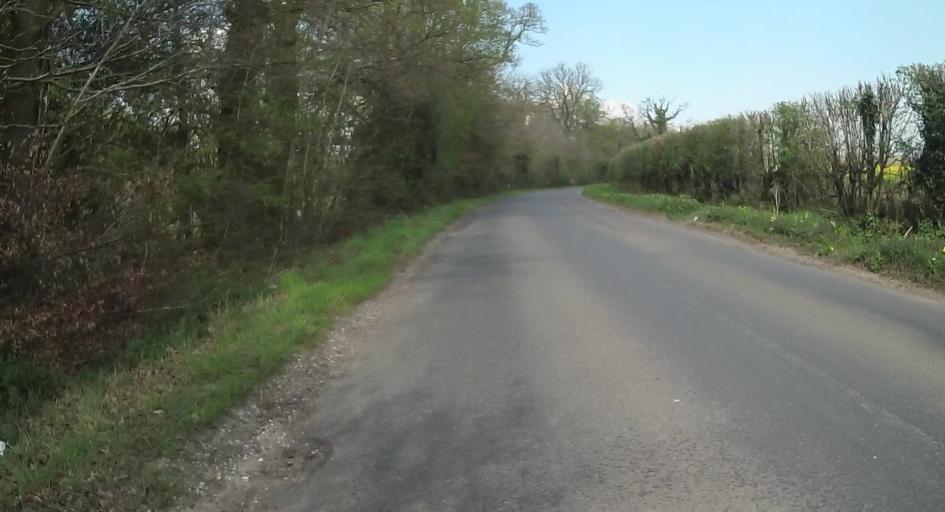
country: GB
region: England
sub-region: Hampshire
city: Basingstoke
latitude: 51.3159
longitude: -1.0820
